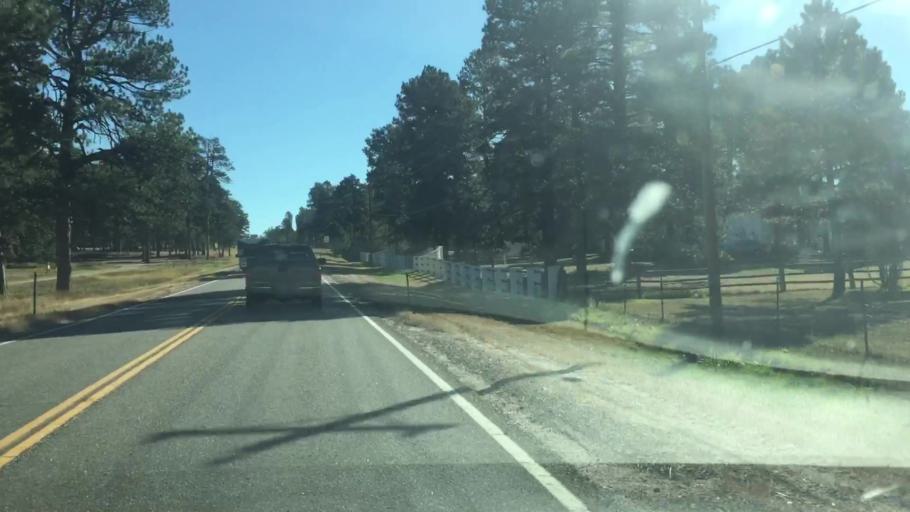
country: US
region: Colorado
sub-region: Elbert County
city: Elizabeth
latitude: 39.3614
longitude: -104.5875
